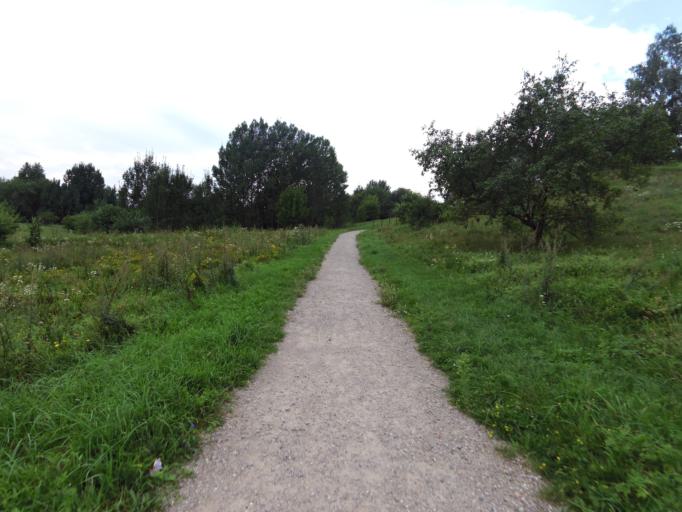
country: LT
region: Vilnius County
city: Seskine
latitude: 54.7147
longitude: 25.2615
